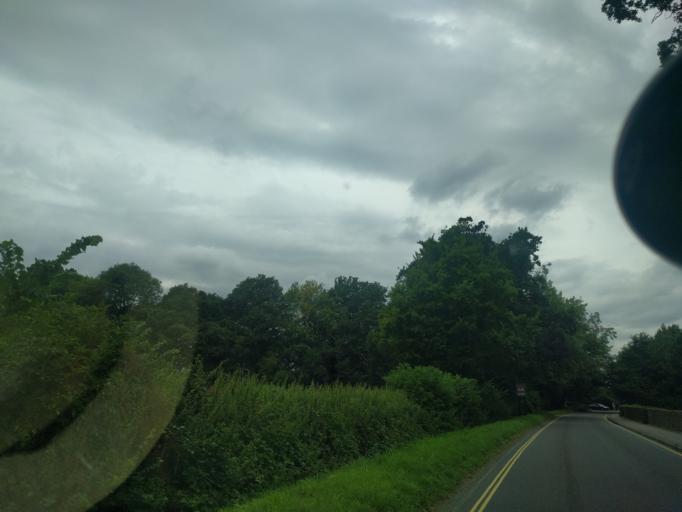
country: GB
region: England
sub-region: Wiltshire
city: Lacock
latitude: 51.4121
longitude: -2.1142
